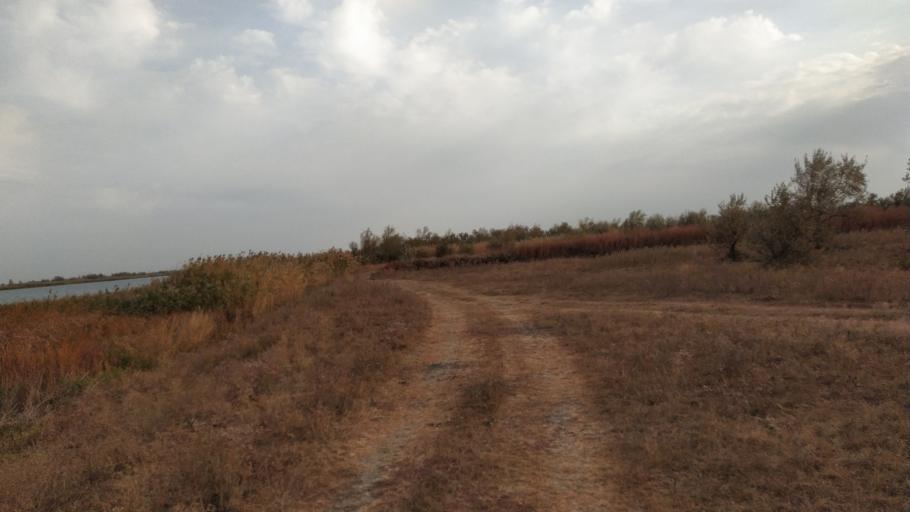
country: RU
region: Rostov
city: Kuleshovka
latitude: 47.1411
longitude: 39.5818
